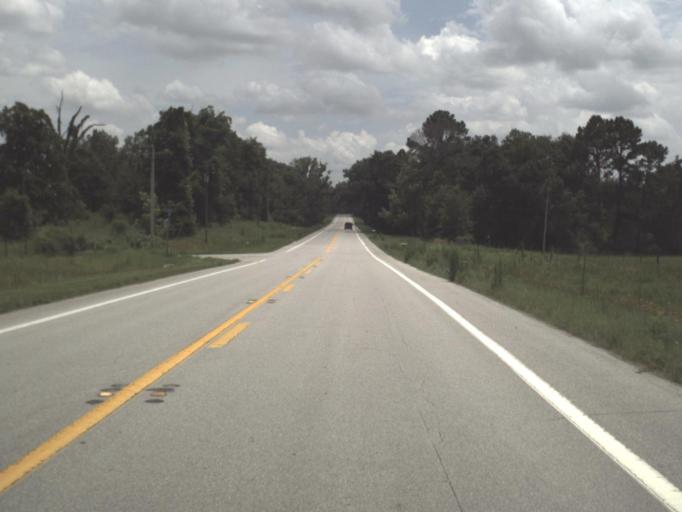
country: US
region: Florida
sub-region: Madison County
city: Madison
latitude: 30.5644
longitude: -83.4296
